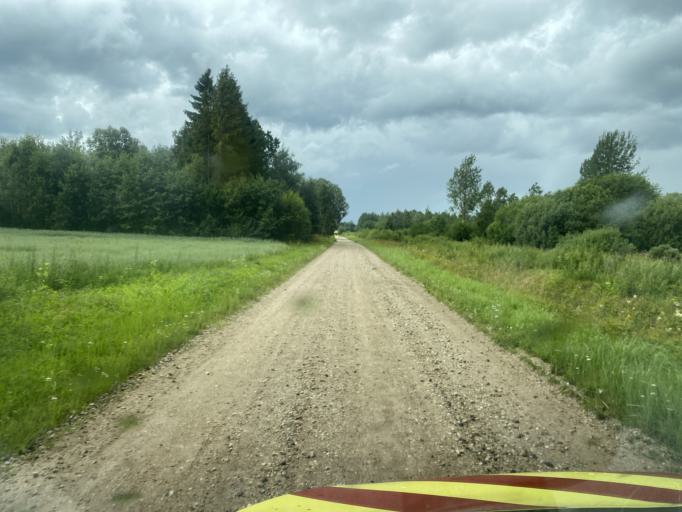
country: EE
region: Valgamaa
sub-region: Torva linn
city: Torva
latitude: 58.0934
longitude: 25.9268
